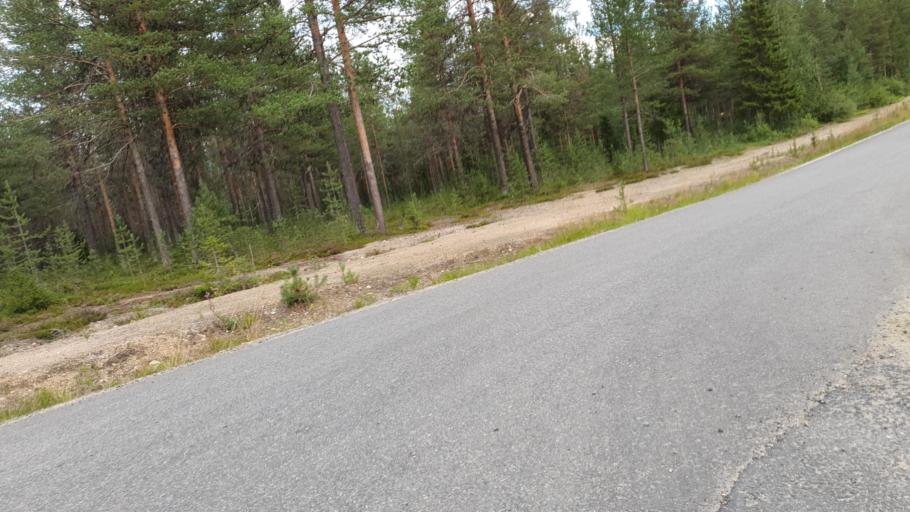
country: FI
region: Lapland
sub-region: Tunturi-Lappi
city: Kolari
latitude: 67.5988
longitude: 24.1375
